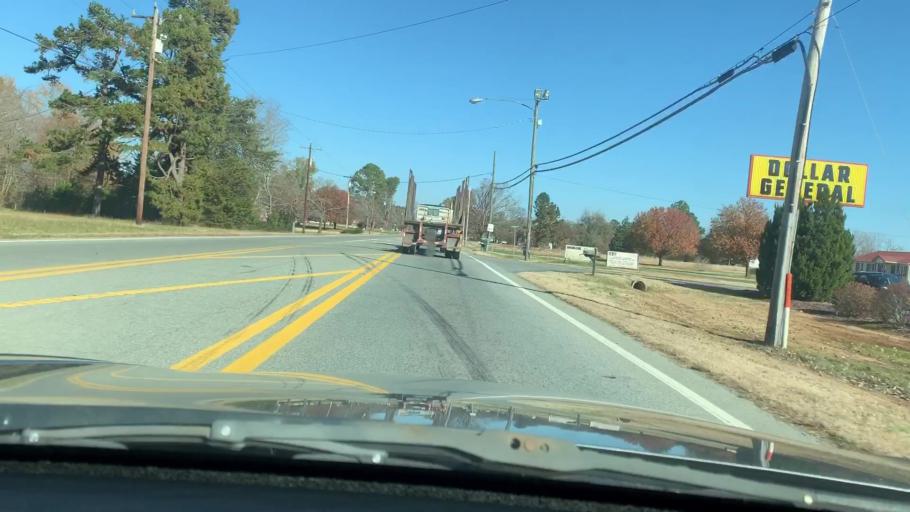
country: US
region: North Carolina
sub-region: Alamance County
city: Green Level
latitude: 36.1189
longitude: -79.3513
